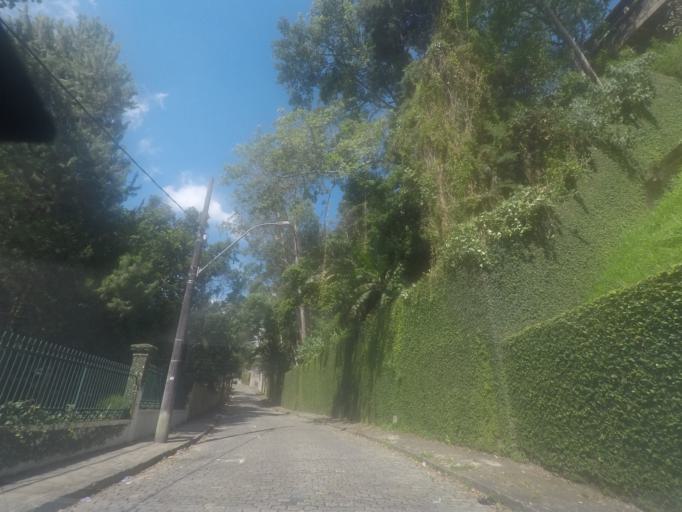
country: BR
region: Rio de Janeiro
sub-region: Petropolis
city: Petropolis
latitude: -22.5100
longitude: -43.1807
